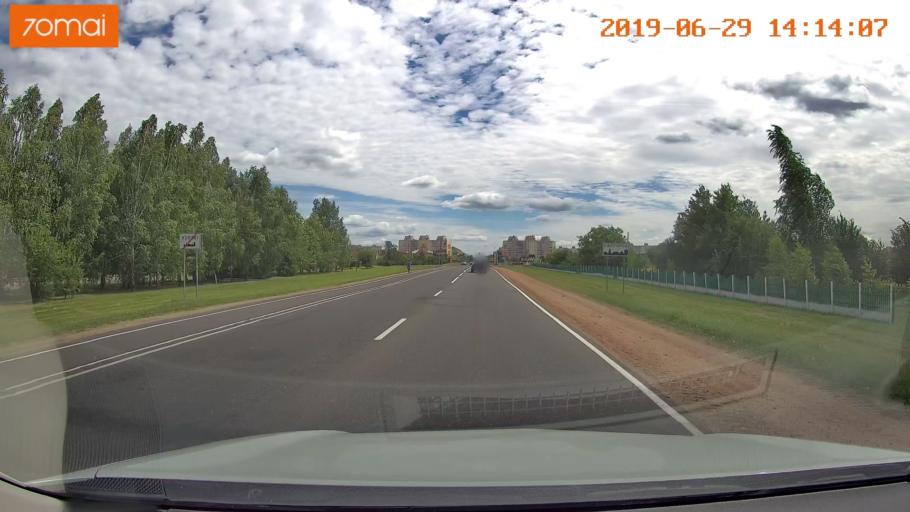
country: BY
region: Minsk
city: Salihorsk
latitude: 52.7976
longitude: 27.5145
